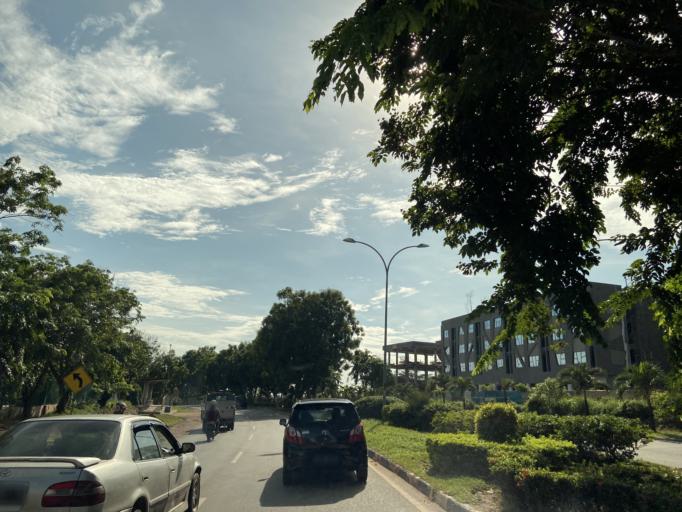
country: SG
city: Singapore
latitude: 1.1211
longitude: 104.0507
